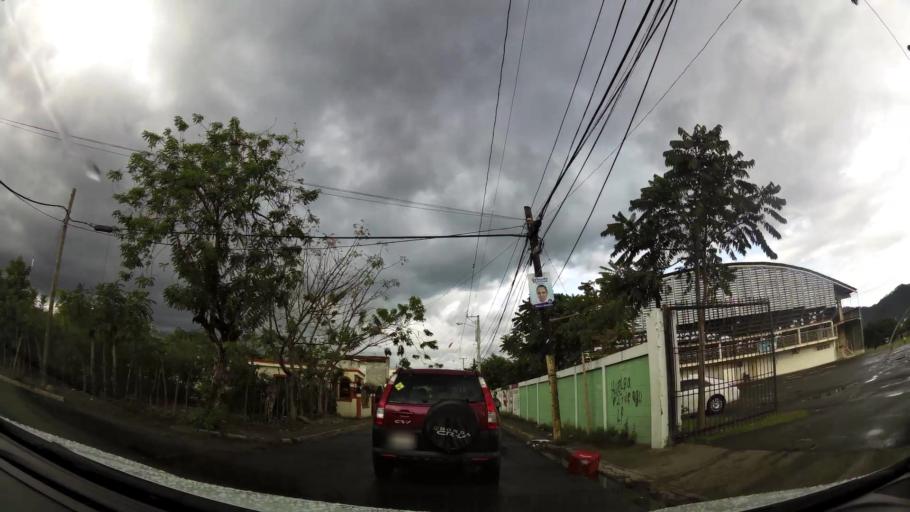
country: DO
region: Monsenor Nouel
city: Bonao
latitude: 18.9322
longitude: -70.3983
